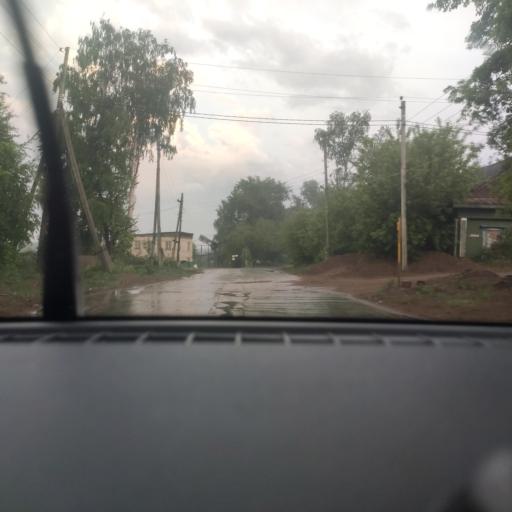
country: RU
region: Perm
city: Nytva
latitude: 57.8920
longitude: 55.4869
